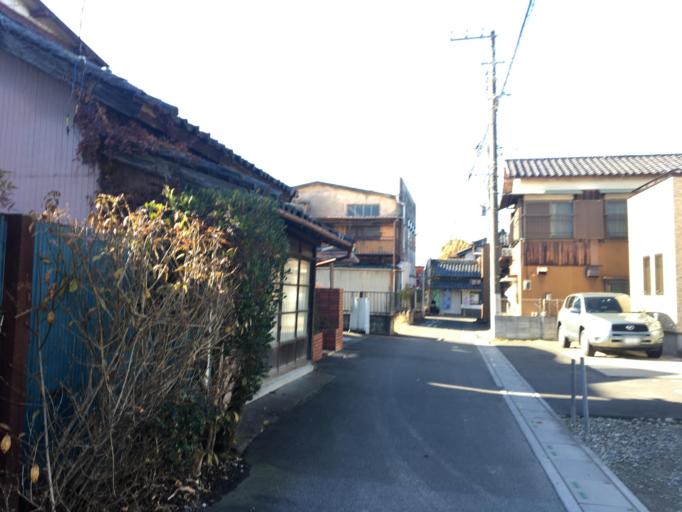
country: JP
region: Saitama
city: Satte
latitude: 36.0774
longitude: 139.7186
